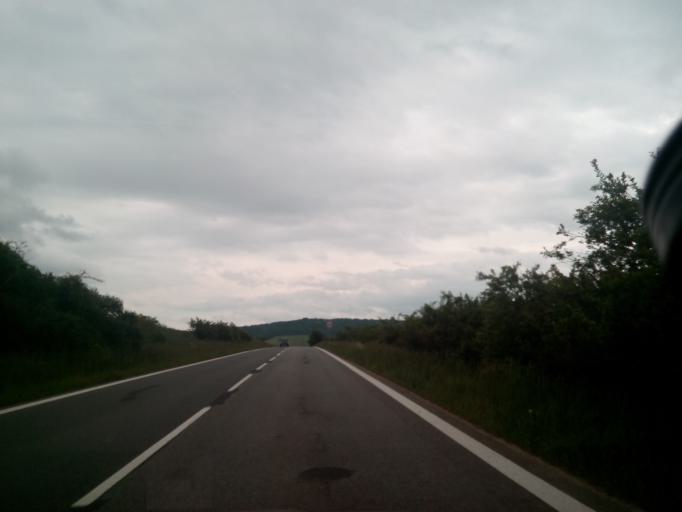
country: SK
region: Kosicky
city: Krompachy
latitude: 48.9944
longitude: 20.9180
